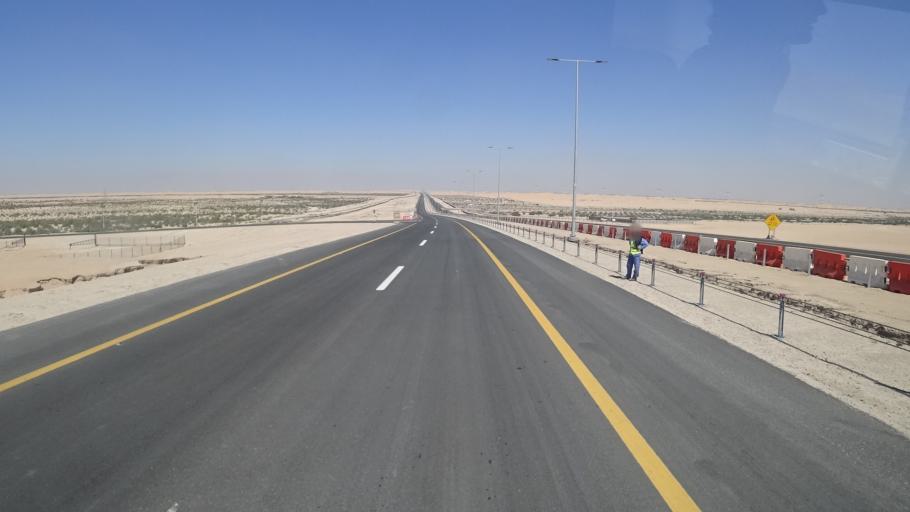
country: AE
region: Abu Dhabi
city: Abu Dhabi
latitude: 24.1336
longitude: 54.8395
